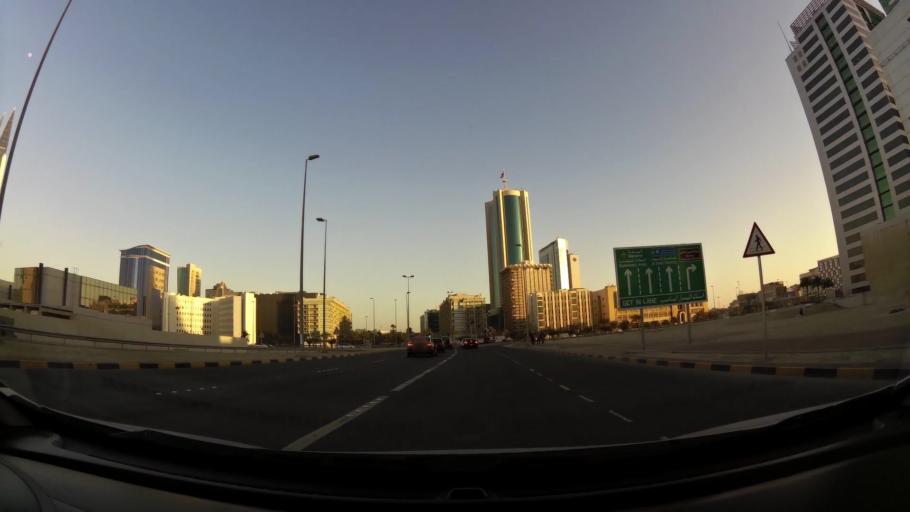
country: BH
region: Manama
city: Manama
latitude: 26.2391
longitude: 50.5759
